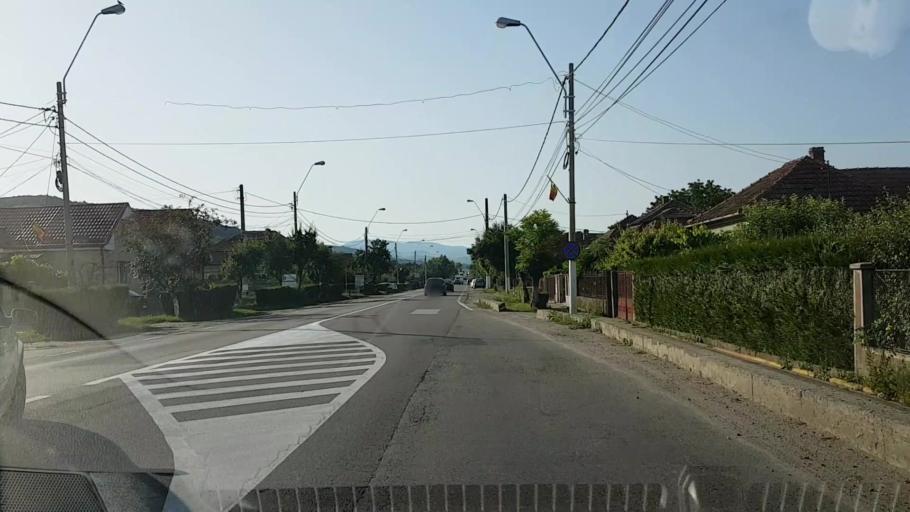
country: RO
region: Alba
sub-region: Municipiul Aiud
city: Aiud
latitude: 46.3167
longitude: 23.7222
